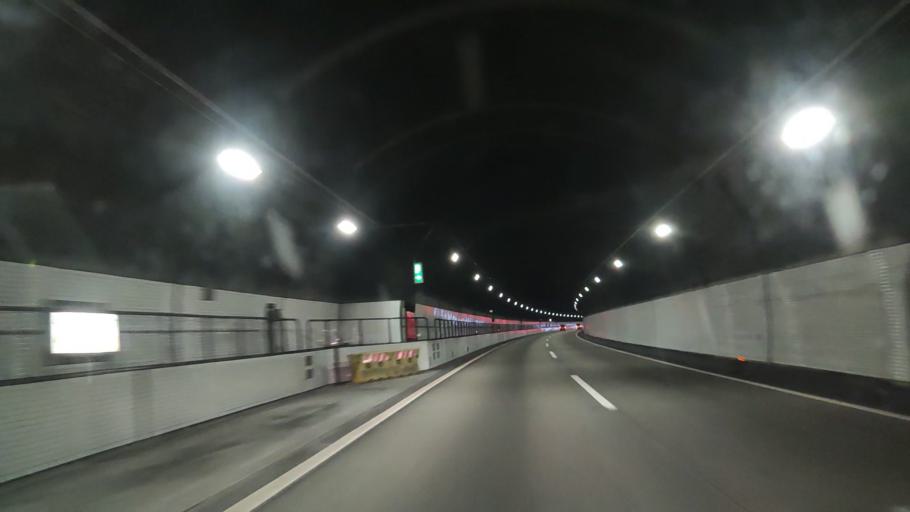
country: JP
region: Ehime
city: Niihama
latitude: 33.9162
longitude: 133.3055
